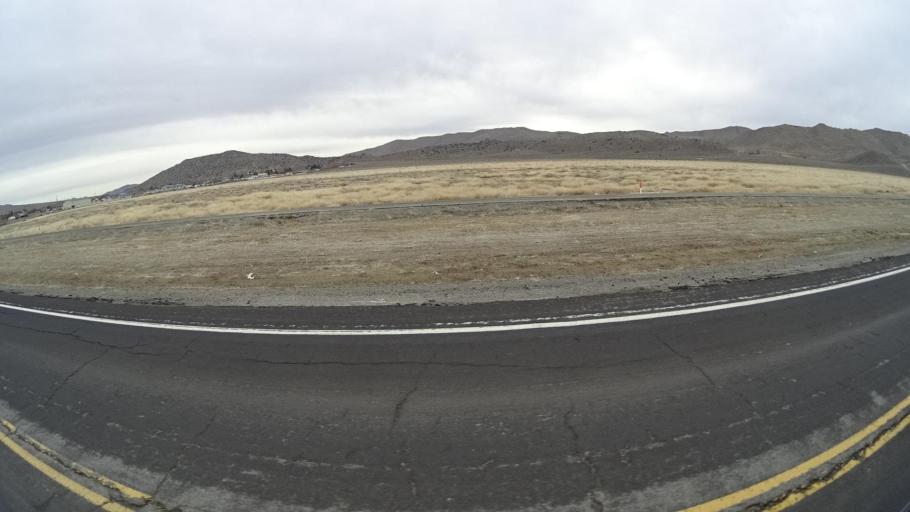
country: US
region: Nevada
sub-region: Washoe County
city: Lemmon Valley
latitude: 39.6558
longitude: -119.8285
